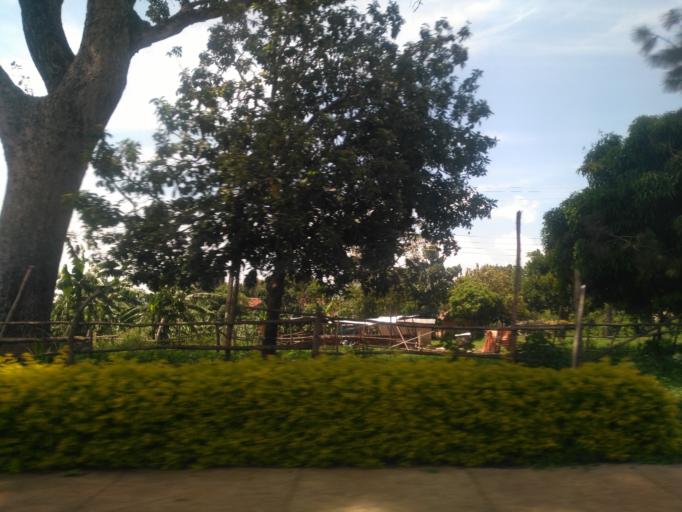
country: UG
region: Central Region
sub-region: Wakiso District
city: Entebbe
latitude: 0.0422
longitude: 32.4620
